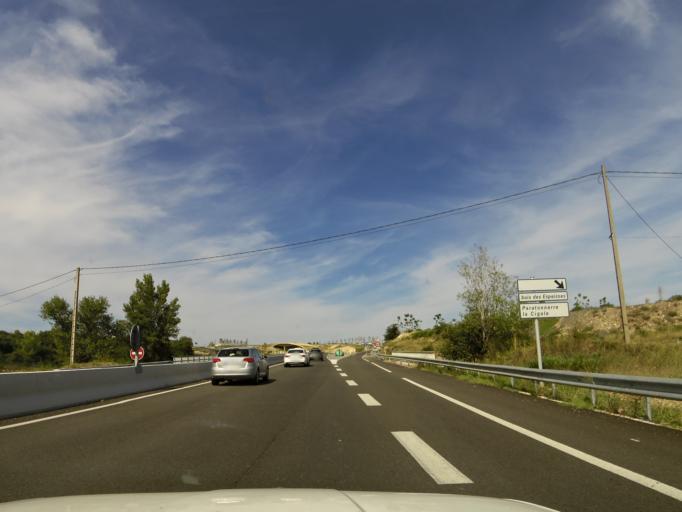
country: FR
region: Languedoc-Roussillon
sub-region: Departement du Gard
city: Nimes
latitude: 43.8540
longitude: 4.3217
